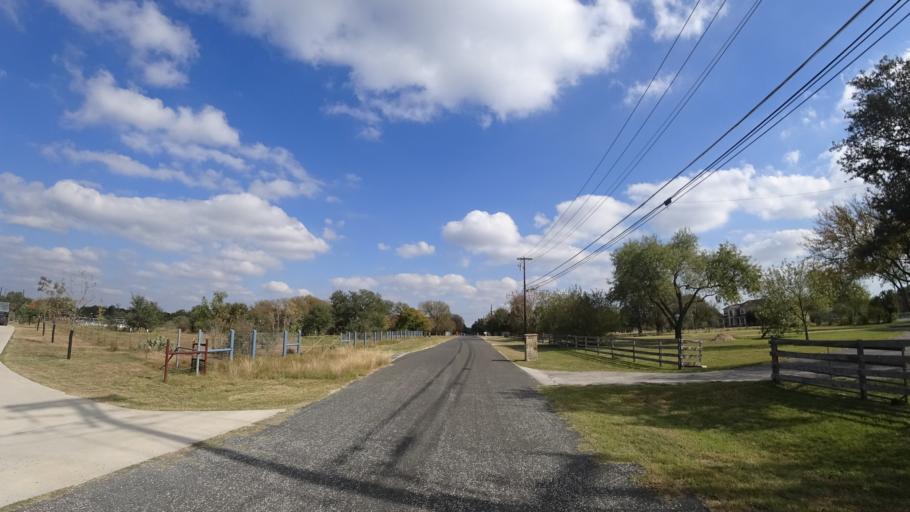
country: US
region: Texas
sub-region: Travis County
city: Shady Hollow
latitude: 30.1759
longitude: -97.8685
